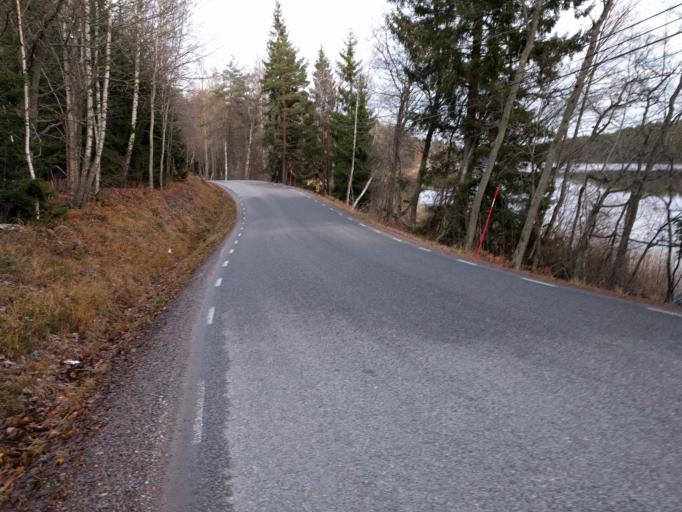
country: SE
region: Stockholm
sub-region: Osterakers Kommun
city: Akersberga
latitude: 59.5918
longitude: 18.3415
